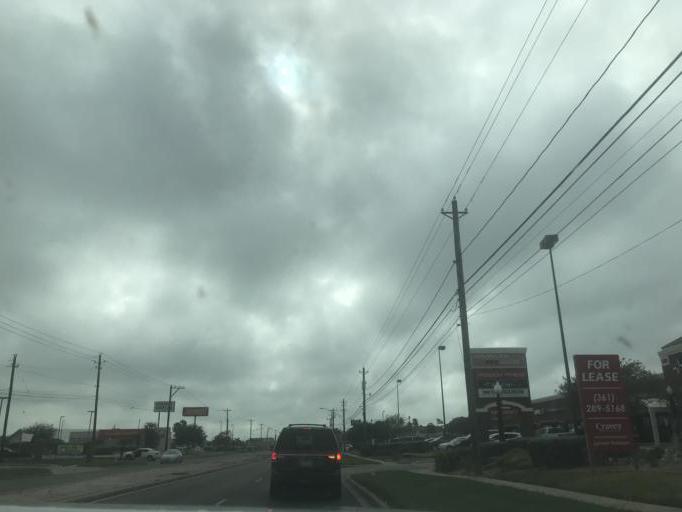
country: US
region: Texas
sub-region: Nueces County
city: Corpus Christi
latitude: 27.6846
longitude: -97.3846
